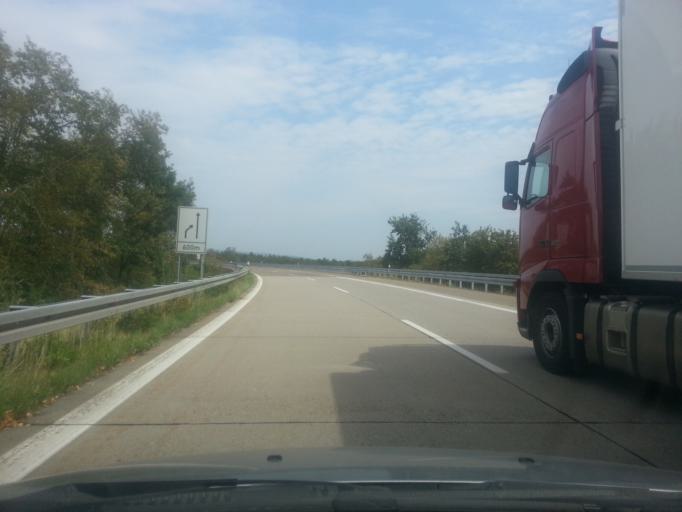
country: DE
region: Baden-Wuerttemberg
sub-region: Karlsruhe Region
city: Hockenheim
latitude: 49.3325
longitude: 8.5538
